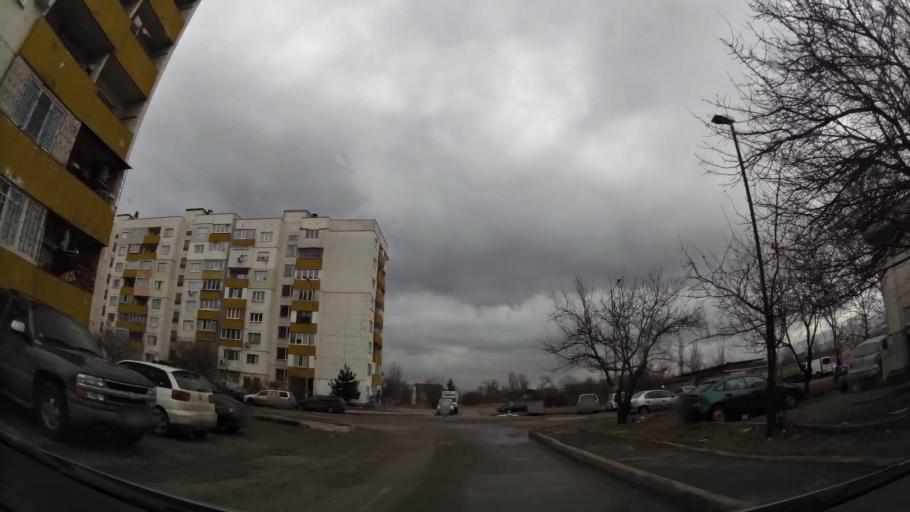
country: BG
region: Sofia-Capital
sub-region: Stolichna Obshtina
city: Sofia
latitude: 42.7229
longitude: 23.2752
